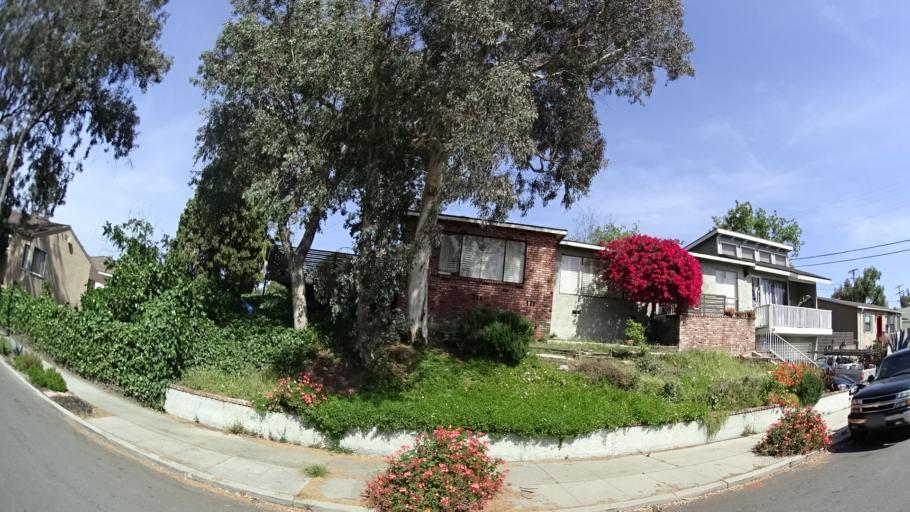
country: US
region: California
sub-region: Los Angeles County
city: Belvedere
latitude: 34.0662
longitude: -118.1845
